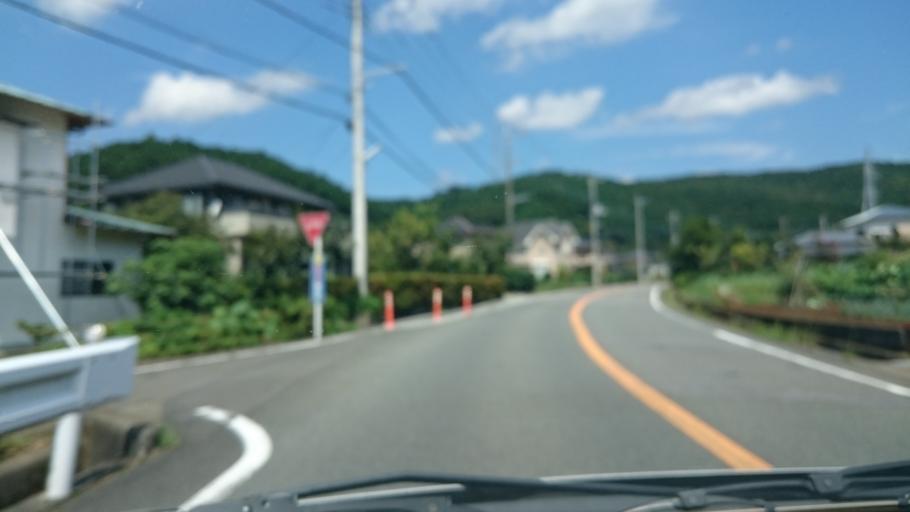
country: JP
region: Shizuoka
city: Gotemba
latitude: 35.2146
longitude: 138.9242
